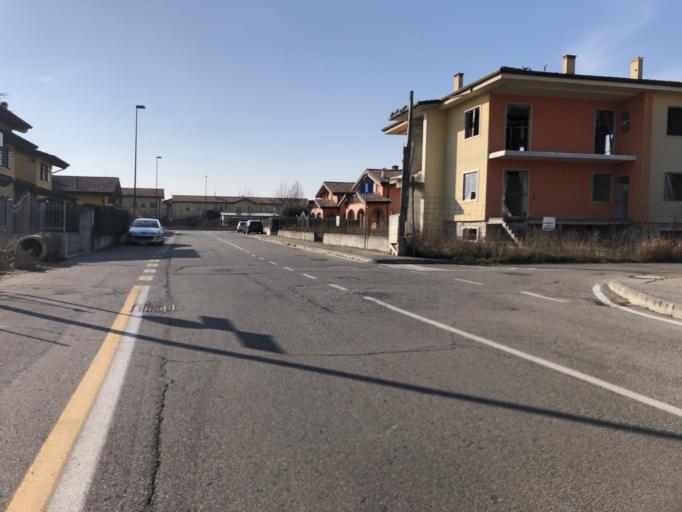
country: IT
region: Veneto
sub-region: Provincia di Verona
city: Lugagnano
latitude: 45.4305
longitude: 10.8793
